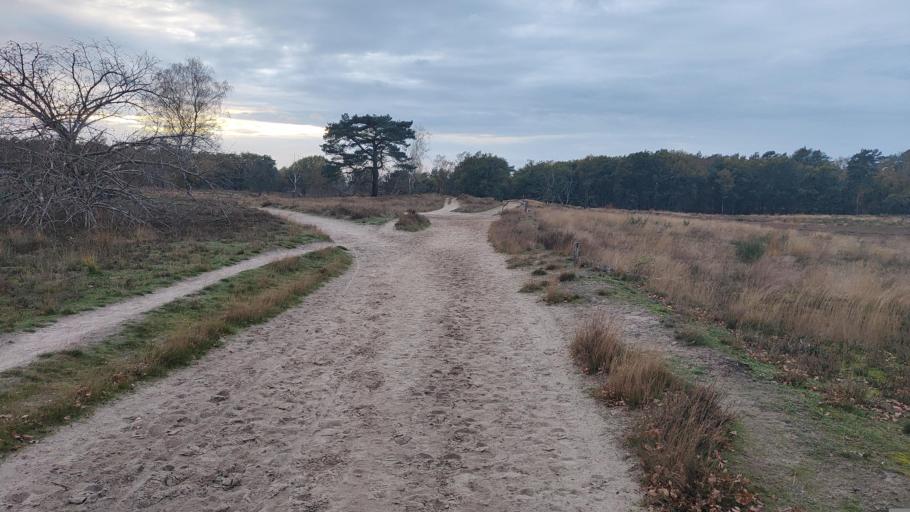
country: NL
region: Limburg
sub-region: Gemeente Roerdalen
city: Herkenbosch
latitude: 51.1704
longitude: 6.1041
